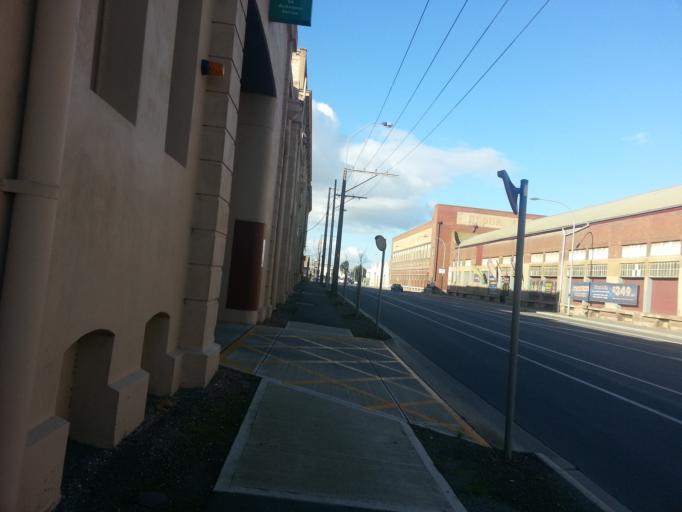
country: AU
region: South Australia
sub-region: Port Adelaide Enfield
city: Birkenhead
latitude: -34.8433
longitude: 138.5115
